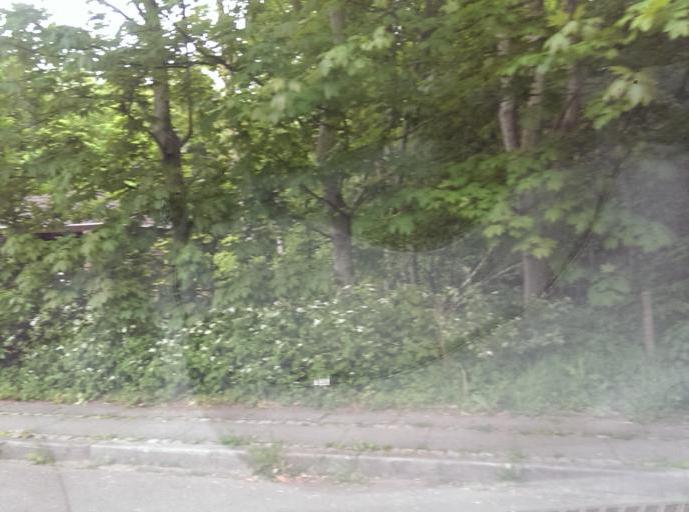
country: DK
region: South Denmark
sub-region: Fano Kommune
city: Nordby
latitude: 55.5233
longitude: 8.3648
